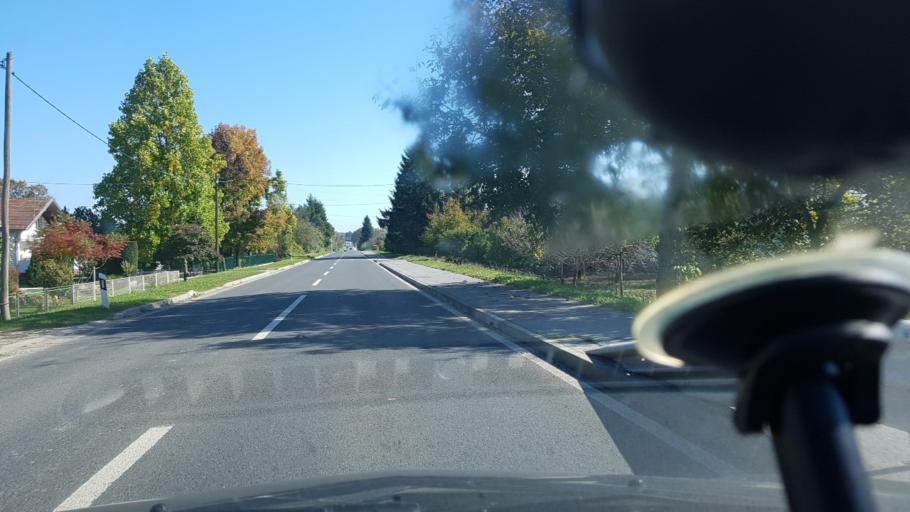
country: HR
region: Zagrebacka
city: Kriz
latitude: 45.7119
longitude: 16.4635
